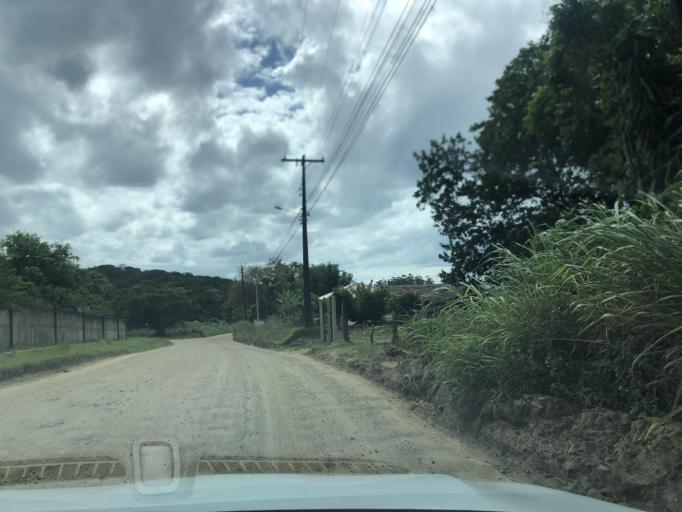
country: BR
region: Santa Catarina
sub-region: Sao Francisco Do Sul
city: Sao Francisco do Sul
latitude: -26.2276
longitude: -48.5894
